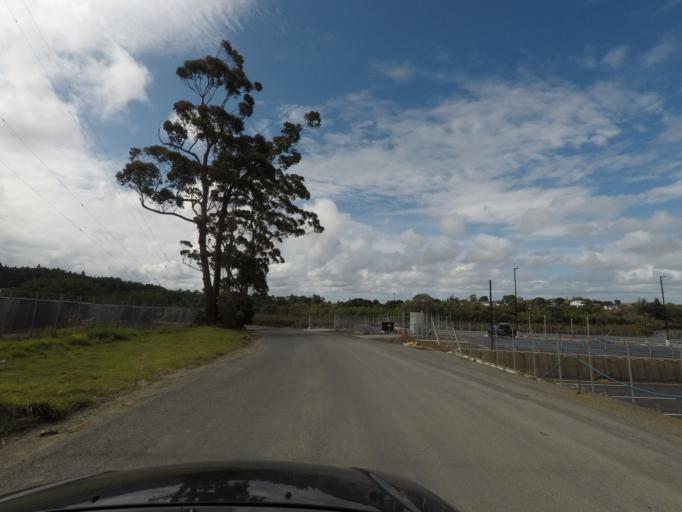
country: NZ
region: Auckland
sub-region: Auckland
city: Rosebank
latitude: -36.8449
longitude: 174.6319
